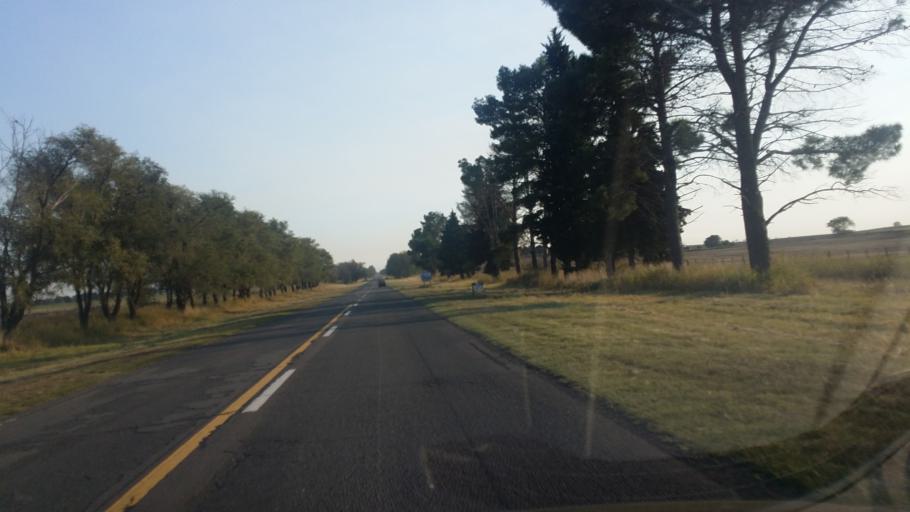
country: AR
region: La Pampa
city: Winifreda
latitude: -36.2056
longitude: -64.2782
